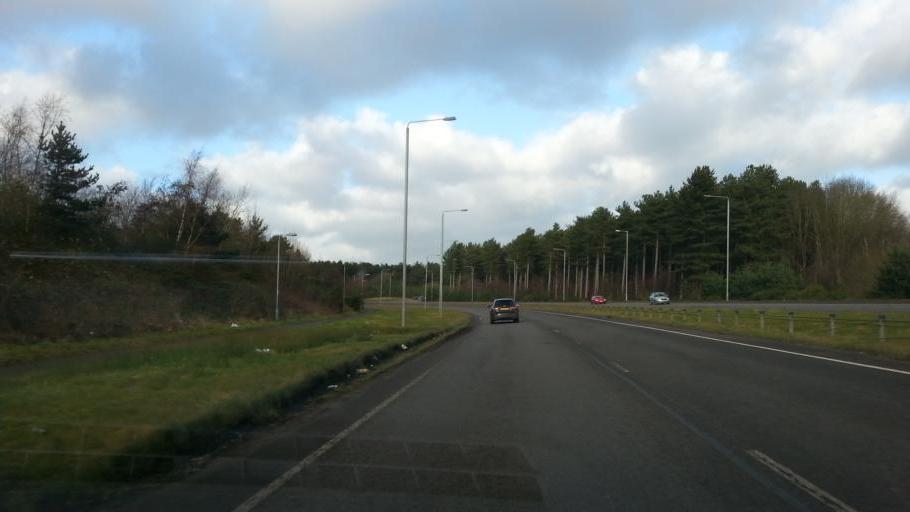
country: GB
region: England
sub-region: Nottinghamshire
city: Rainworth
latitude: 53.1278
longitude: -1.1259
